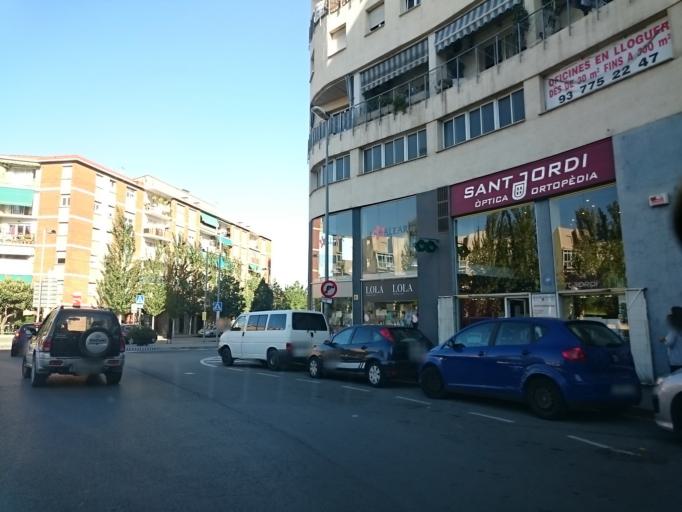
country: ES
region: Catalonia
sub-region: Provincia de Barcelona
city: Martorell
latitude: 41.4772
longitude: 1.9176
